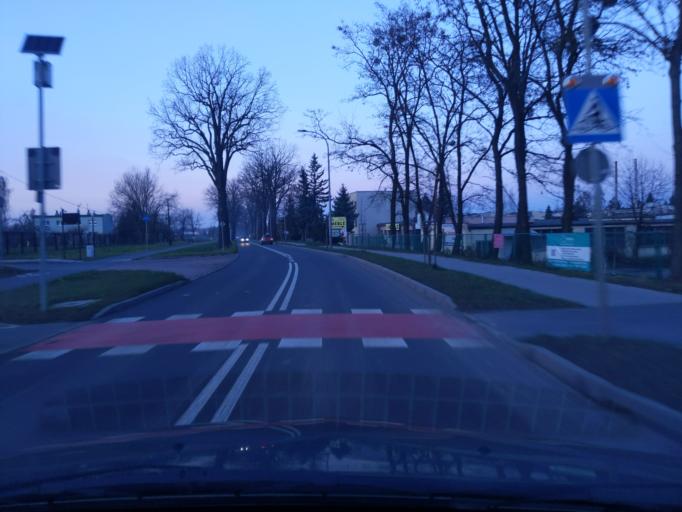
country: PL
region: Silesian Voivodeship
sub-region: Powiat pszczynski
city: Pszczyna
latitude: 49.9606
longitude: 18.9333
